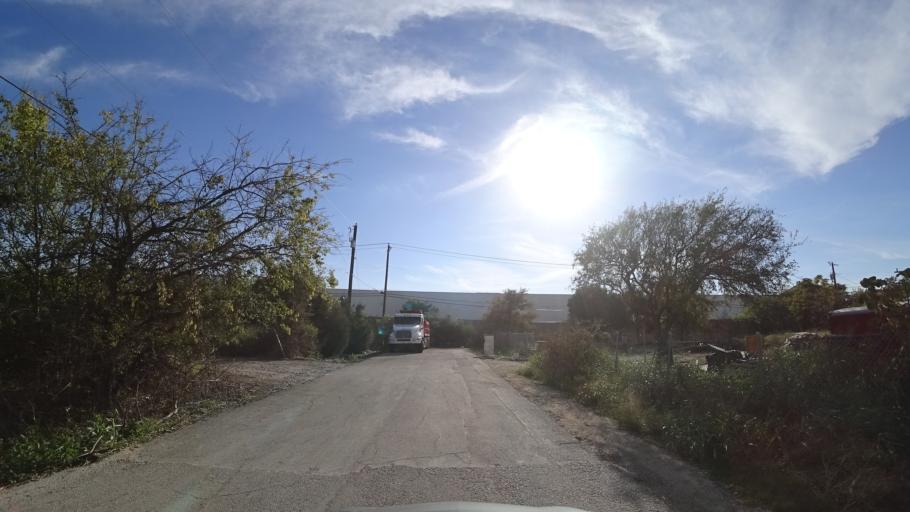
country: US
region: Texas
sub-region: Travis County
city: Wells Branch
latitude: 30.4711
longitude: -97.6858
